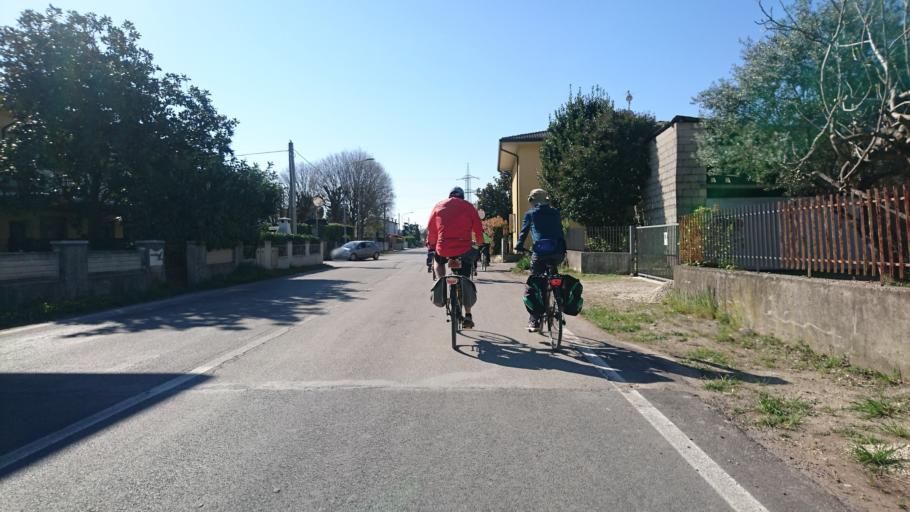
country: IT
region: Veneto
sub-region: Provincia di Vicenza
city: San Zeno-San Giuseppe
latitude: 45.7323
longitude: 11.7429
